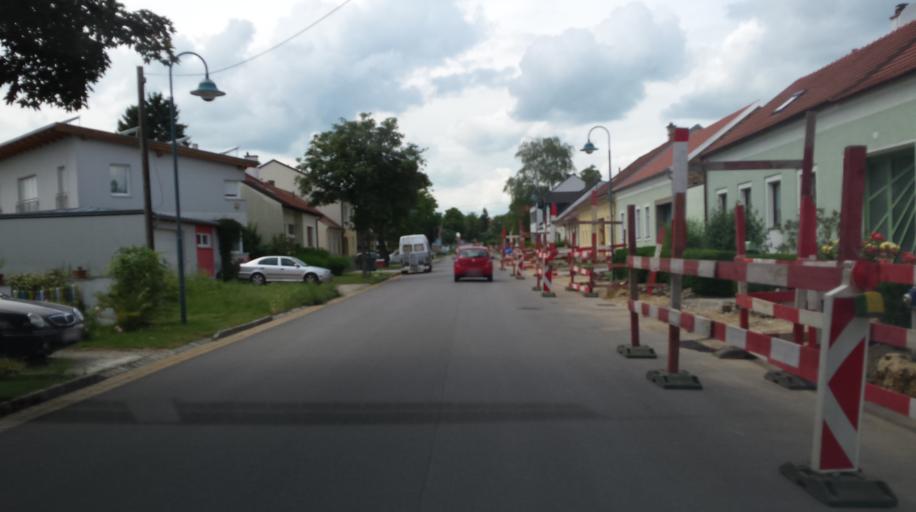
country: AT
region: Lower Austria
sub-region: Politischer Bezirk Mistelbach
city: Wolkersdorf im Weinviertel
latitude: 48.3754
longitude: 16.5193
